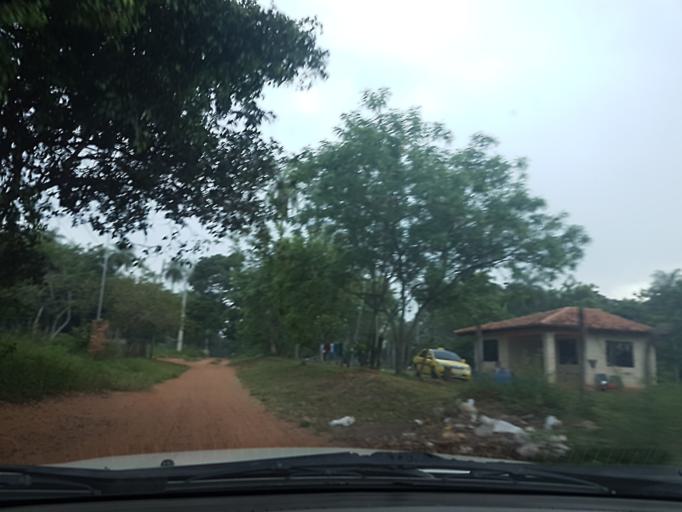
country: PY
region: Central
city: Limpio
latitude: -25.2411
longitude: -57.4608
